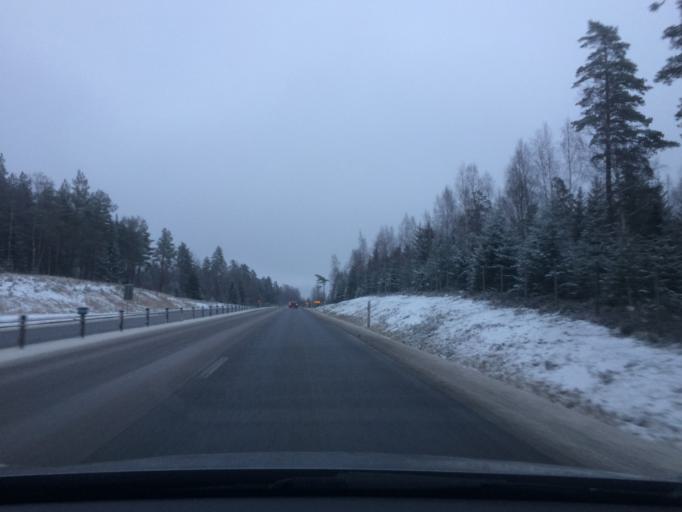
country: SE
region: Kronoberg
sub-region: Vaxjo Kommun
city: Vaexjoe
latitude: 56.8841
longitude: 14.8583
